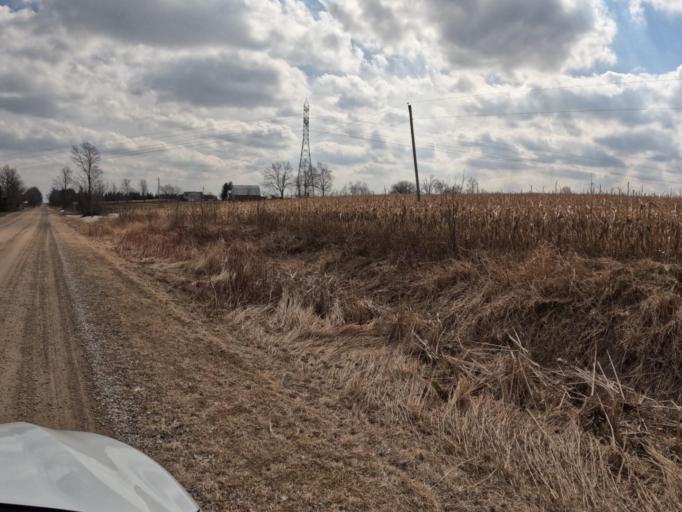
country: CA
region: Ontario
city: Shelburne
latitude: 43.9558
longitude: -80.2807
